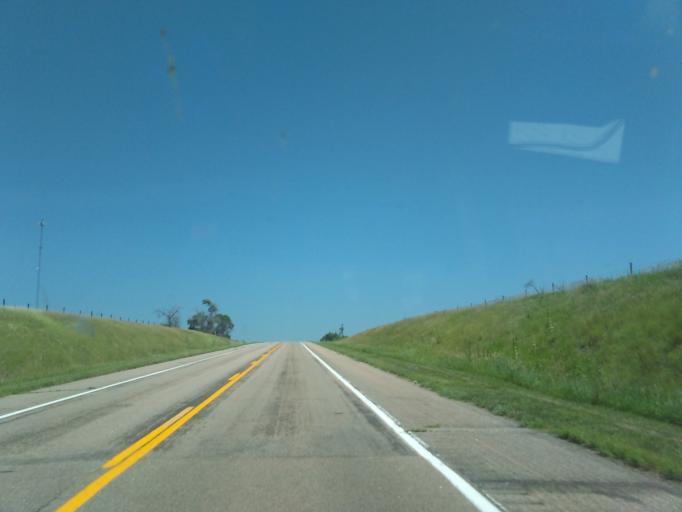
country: US
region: Nebraska
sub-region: Frontier County
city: Stockville
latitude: 40.5958
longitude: -100.6295
